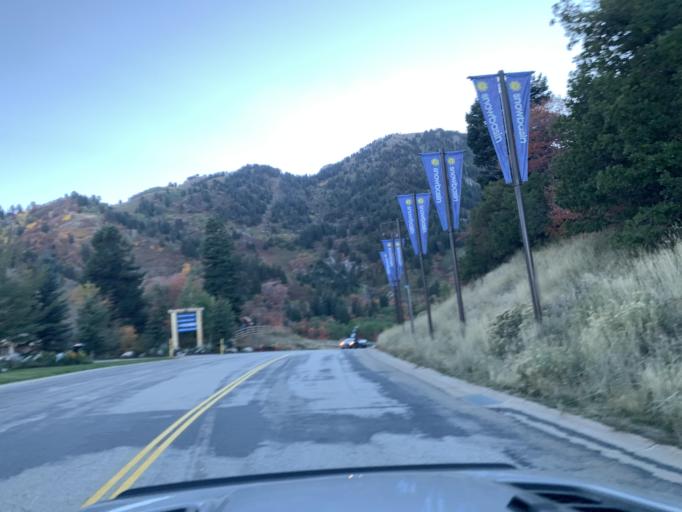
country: US
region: Utah
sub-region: Weber County
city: Uintah
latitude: 41.2173
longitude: -111.8579
